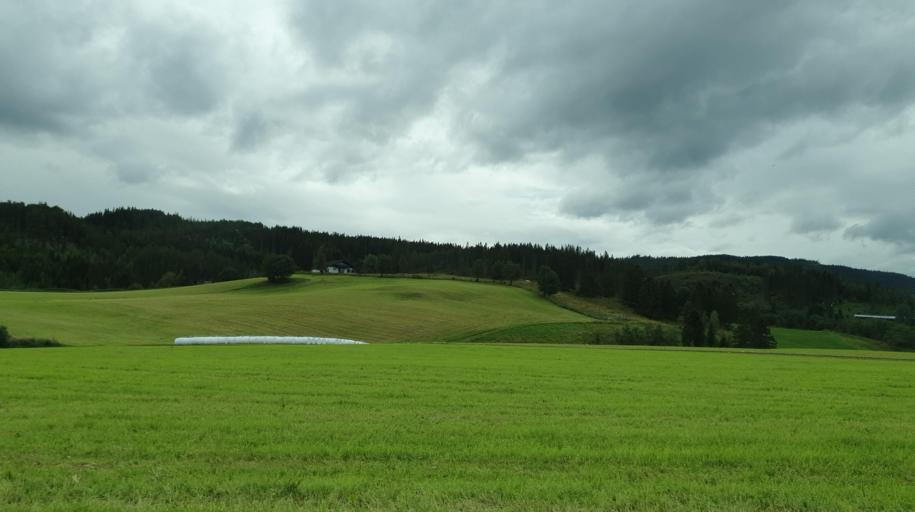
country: NO
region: Nord-Trondelag
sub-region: Stjordal
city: Stjordalshalsen
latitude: 63.4144
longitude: 10.9626
